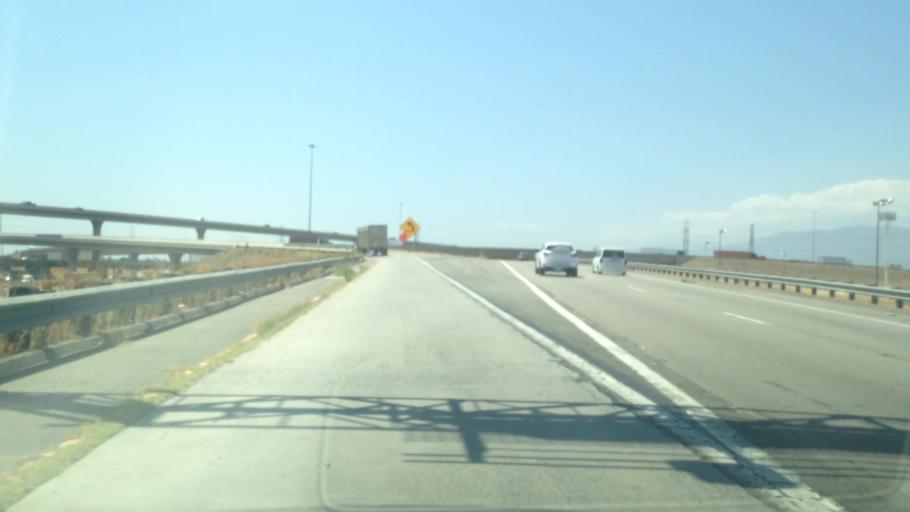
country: US
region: California
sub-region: Riverside County
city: Mira Loma
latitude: 34.0211
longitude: -117.5461
